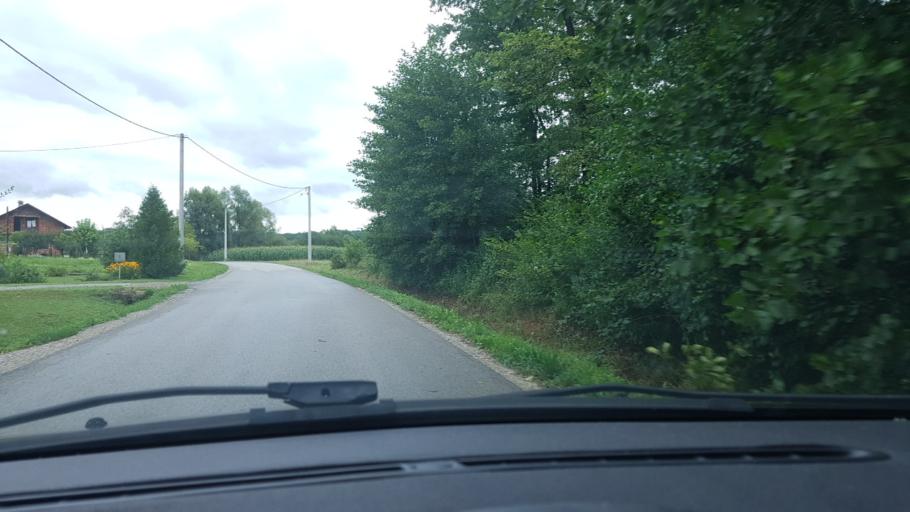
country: HR
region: Karlovacka
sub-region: Grad Karlovac
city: Karlovac
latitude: 45.5671
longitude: 15.5455
